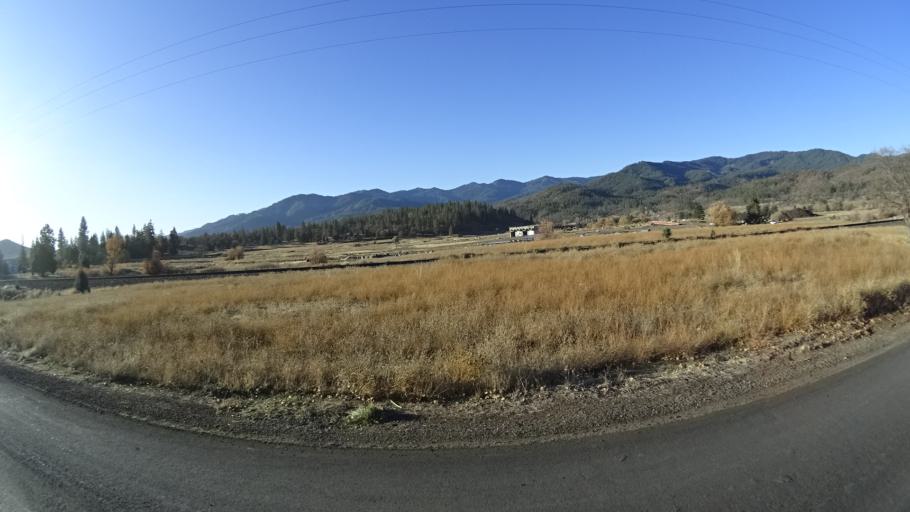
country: US
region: Oregon
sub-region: Jackson County
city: Ashland
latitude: 41.9974
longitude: -122.6287
